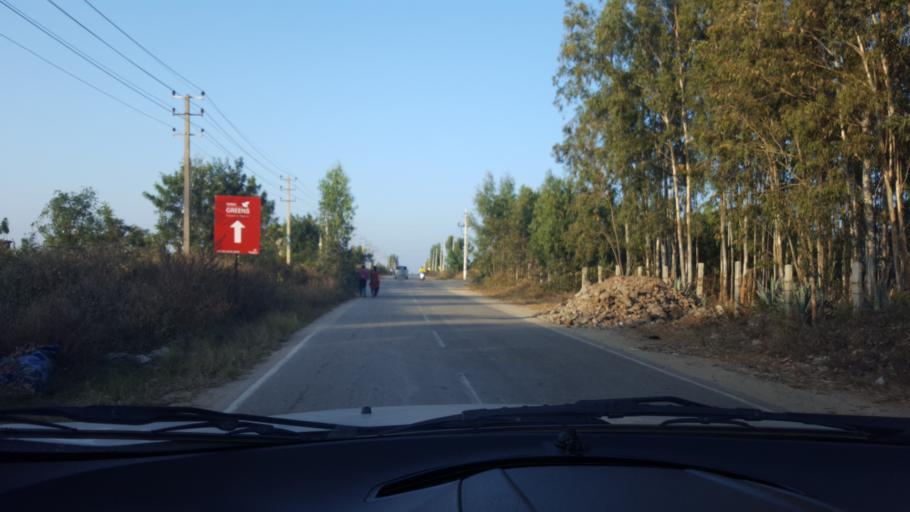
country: IN
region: Karnataka
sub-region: Bangalore Urban
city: Yelahanka
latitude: 13.1889
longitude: 77.6004
